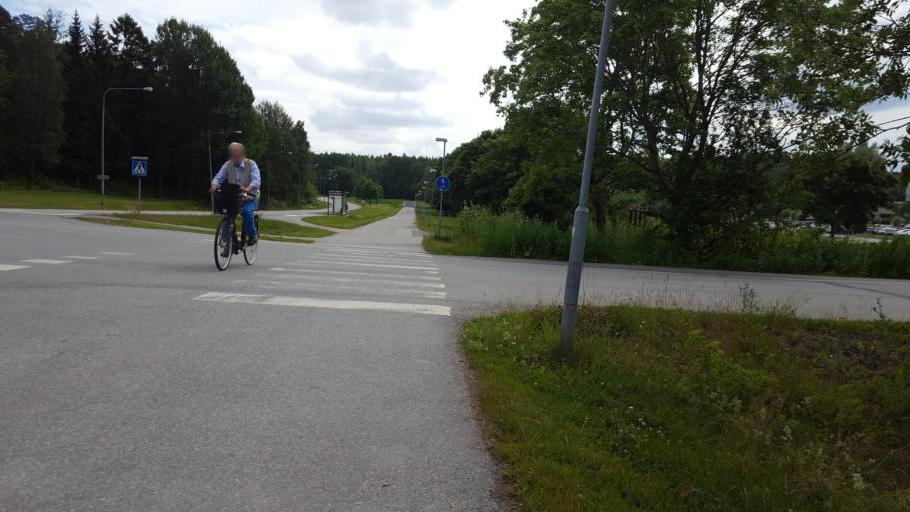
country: SE
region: Stockholm
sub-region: Upplands Vasby Kommun
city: Upplands Vaesby
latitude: 59.5099
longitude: 17.9000
